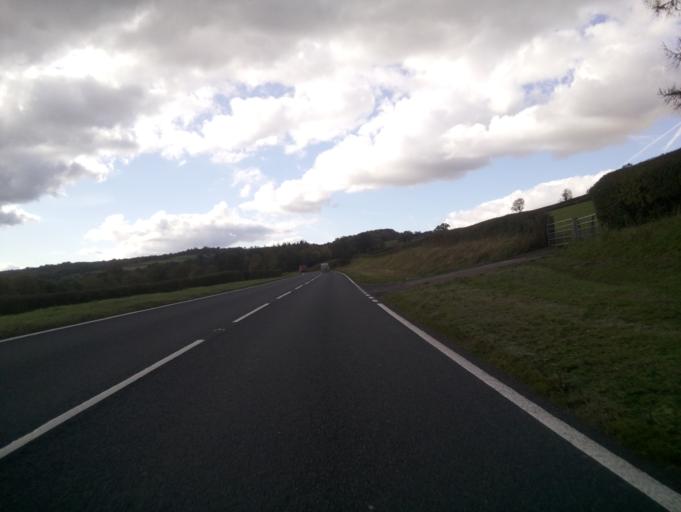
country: GB
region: Wales
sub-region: Sir Powys
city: Brecon
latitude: 51.9335
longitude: -3.4360
